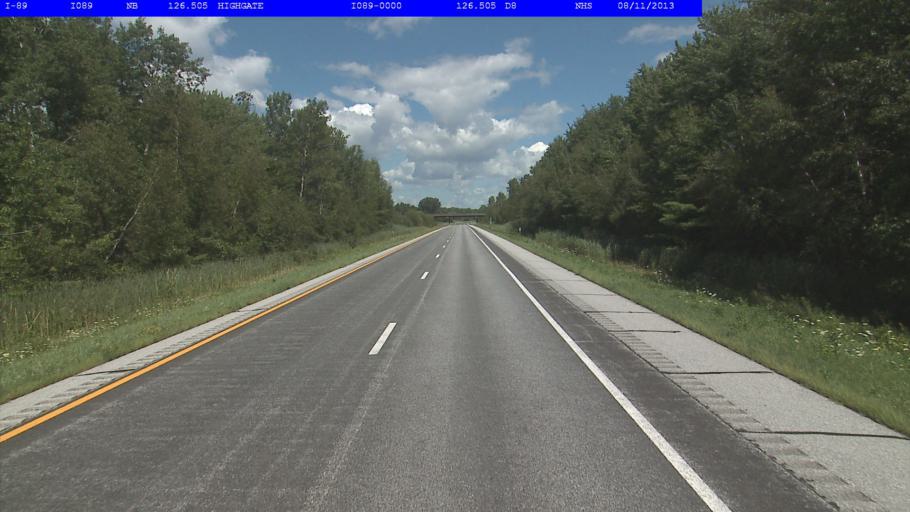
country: US
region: Vermont
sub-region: Franklin County
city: Swanton
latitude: 44.9662
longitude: -73.1059
